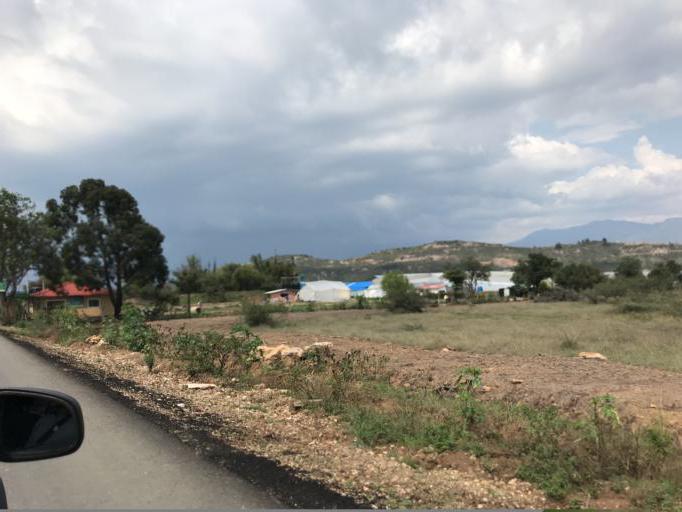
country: CO
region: Boyaca
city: Sutamarchan
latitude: 5.6360
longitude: -73.5998
